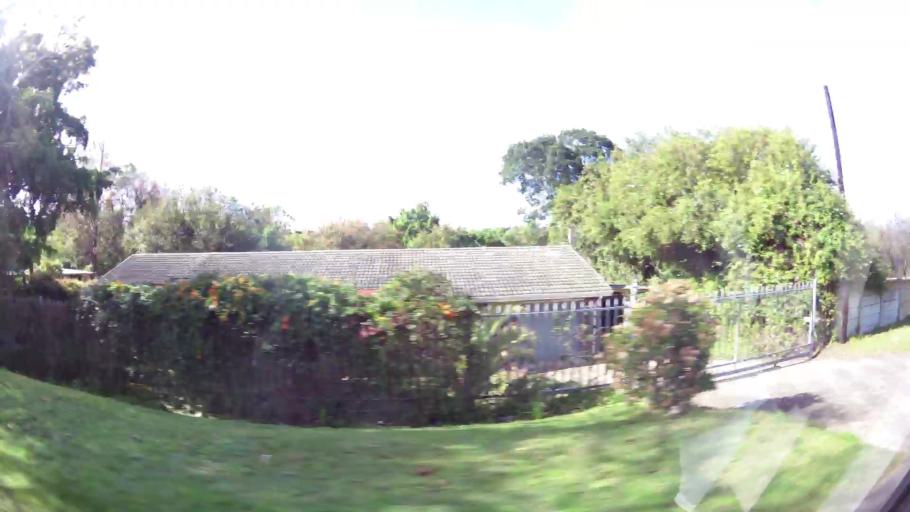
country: ZA
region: Western Cape
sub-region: Eden District Municipality
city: Knysna
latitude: -34.0429
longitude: 23.0726
